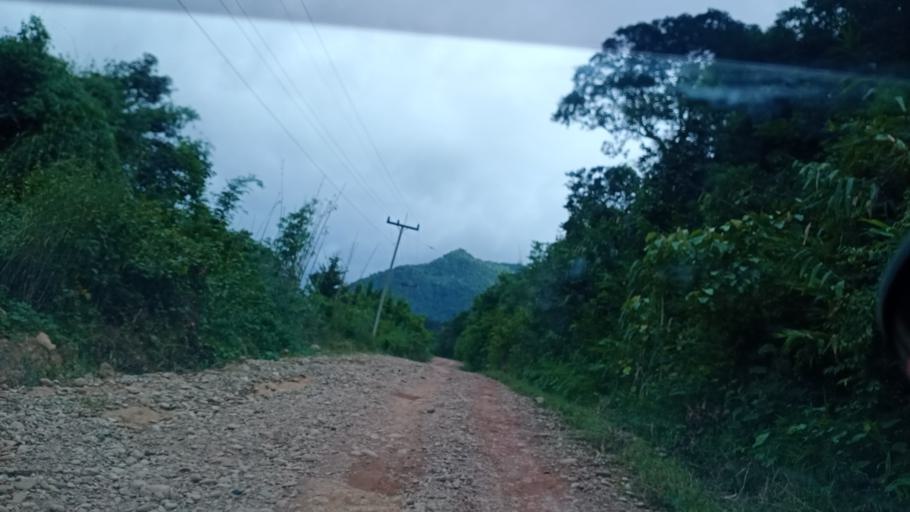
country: TH
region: Changwat Bueng Kan
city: Pak Khat
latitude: 18.7225
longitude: 103.2474
